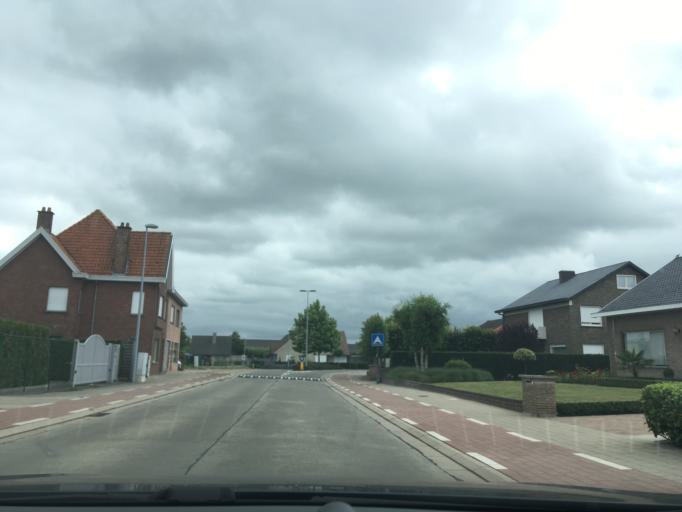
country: BE
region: Flanders
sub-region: Provincie West-Vlaanderen
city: Wingene
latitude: 51.0569
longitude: 3.2732
